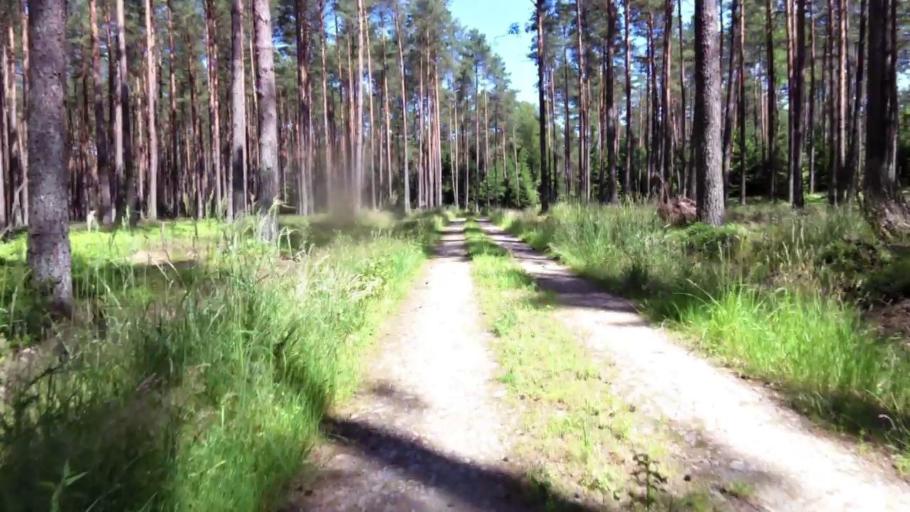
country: PL
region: West Pomeranian Voivodeship
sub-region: Powiat bialogardzki
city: Tychowo
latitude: 53.9126
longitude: 16.1178
